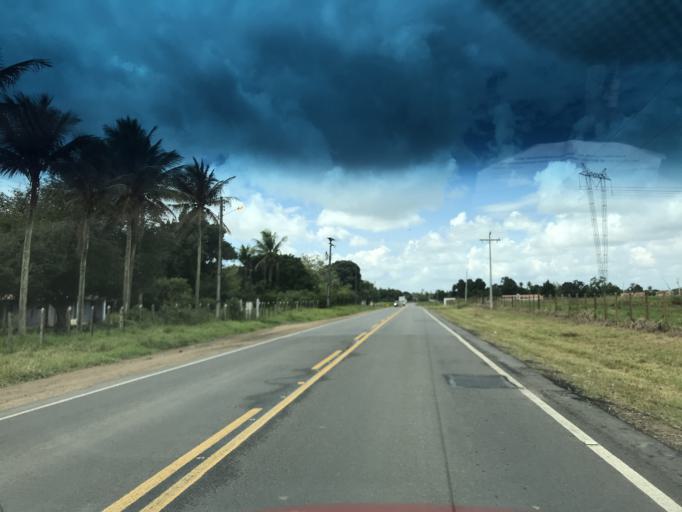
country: BR
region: Bahia
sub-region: Conceicao Do Almeida
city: Conceicao do Almeida
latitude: -12.7240
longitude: -39.2070
